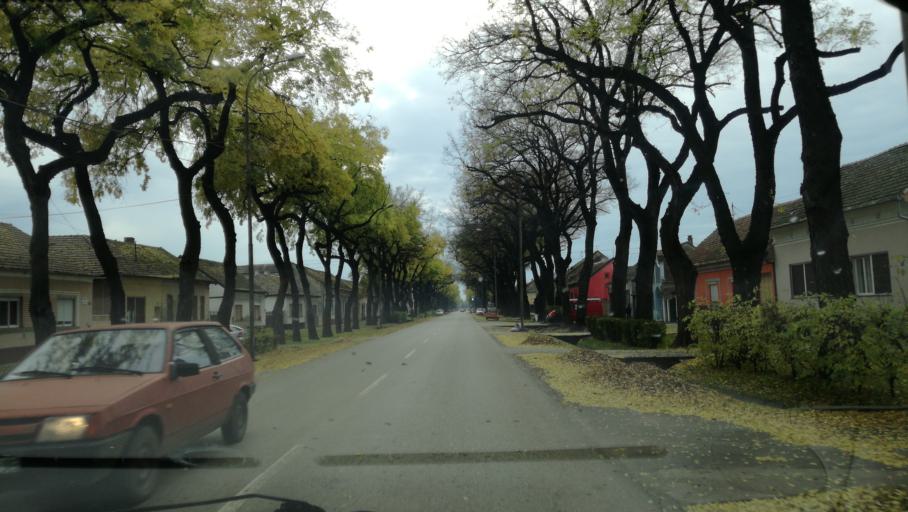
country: RS
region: Autonomna Pokrajina Vojvodina
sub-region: Severnobanatski Okrug
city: Kikinda
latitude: 45.8387
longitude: 20.4799
